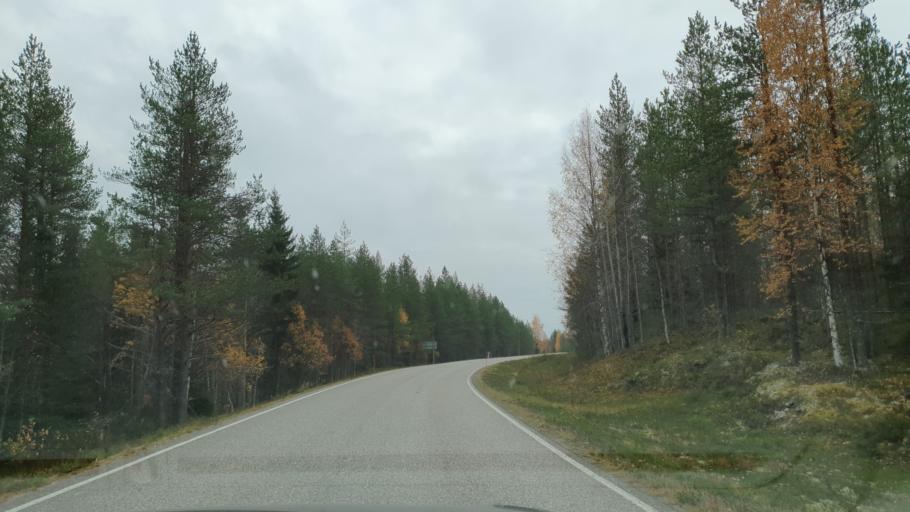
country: FI
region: Kainuu
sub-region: Kajaani
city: Paltamo
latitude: 64.6489
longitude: 27.9647
